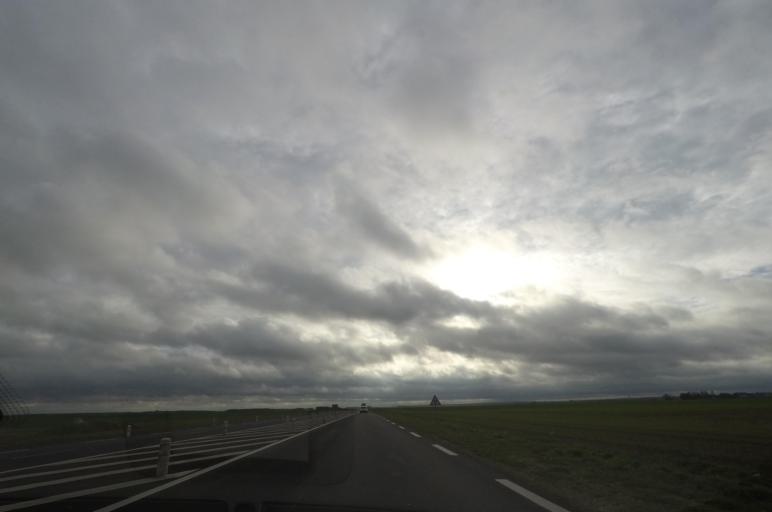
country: FR
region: Centre
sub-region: Departement du Loir-et-Cher
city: Herbault
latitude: 47.7127
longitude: 1.1628
